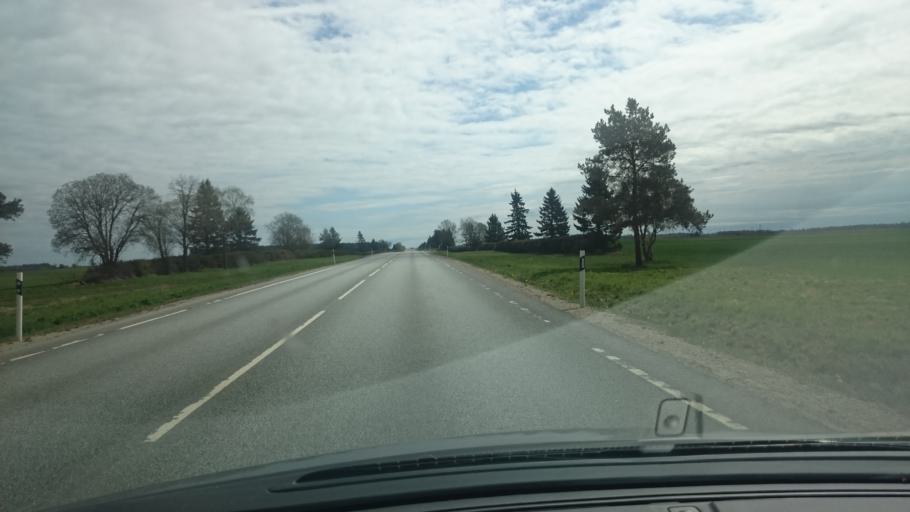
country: EE
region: Laeaene-Virumaa
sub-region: Haljala vald
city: Haljala
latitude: 59.4204
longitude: 26.3018
